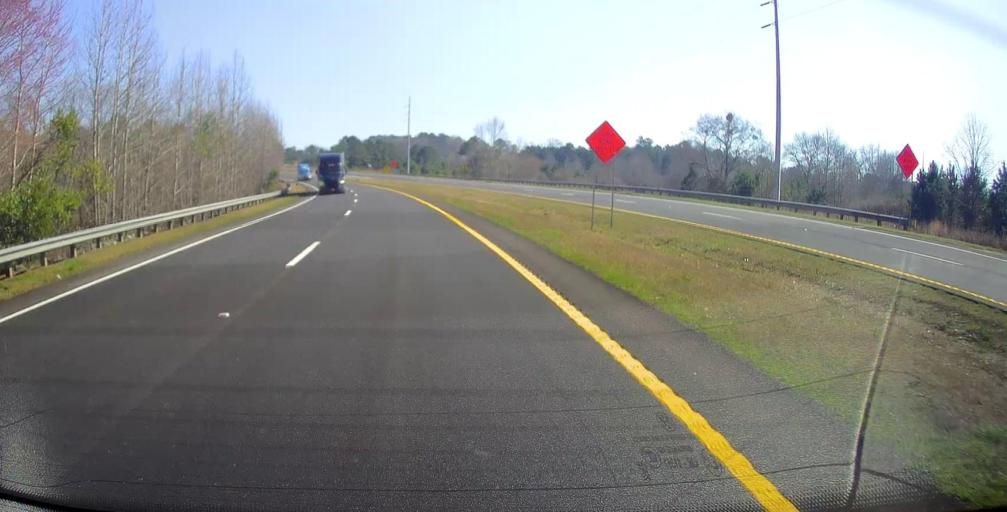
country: US
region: Georgia
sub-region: Houston County
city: Perry
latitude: 32.4883
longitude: -83.7353
